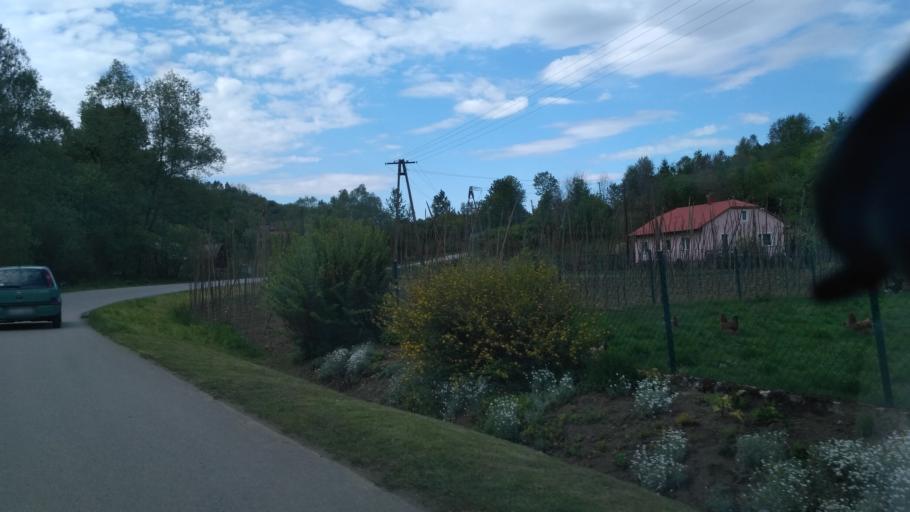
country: PL
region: Subcarpathian Voivodeship
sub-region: Powiat przemyski
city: Przedmiescie Dubieckie
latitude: 49.8501
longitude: 22.3556
